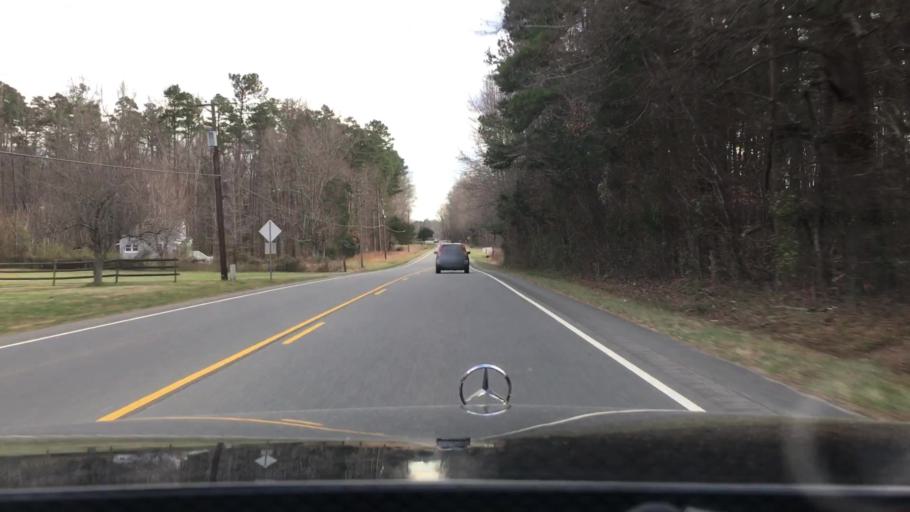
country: US
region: North Carolina
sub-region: Orange County
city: Hillsborough
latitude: 36.1415
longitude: -79.1216
